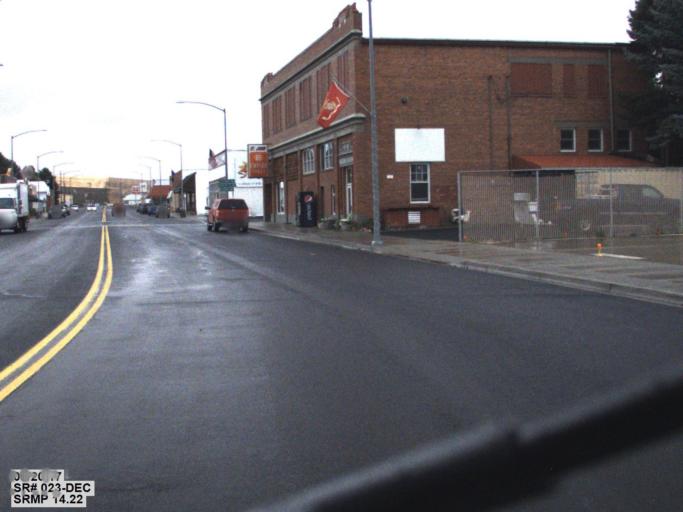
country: US
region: Washington
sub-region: Whitman County
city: Colfax
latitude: 47.0919
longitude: -117.5826
